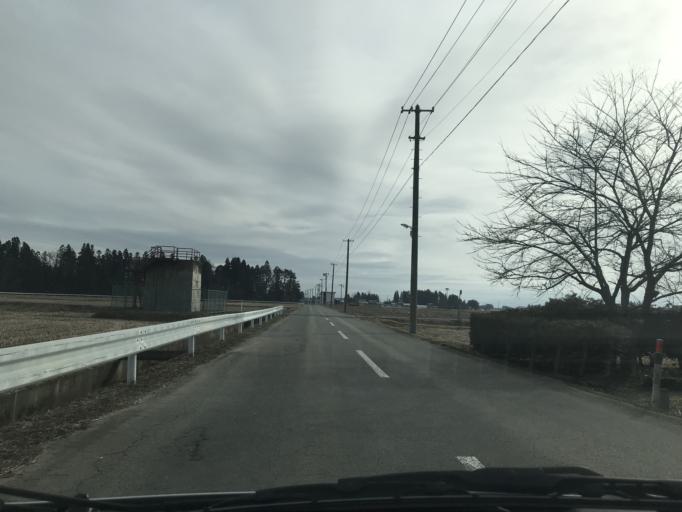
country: JP
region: Iwate
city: Hanamaki
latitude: 39.4049
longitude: 141.0765
